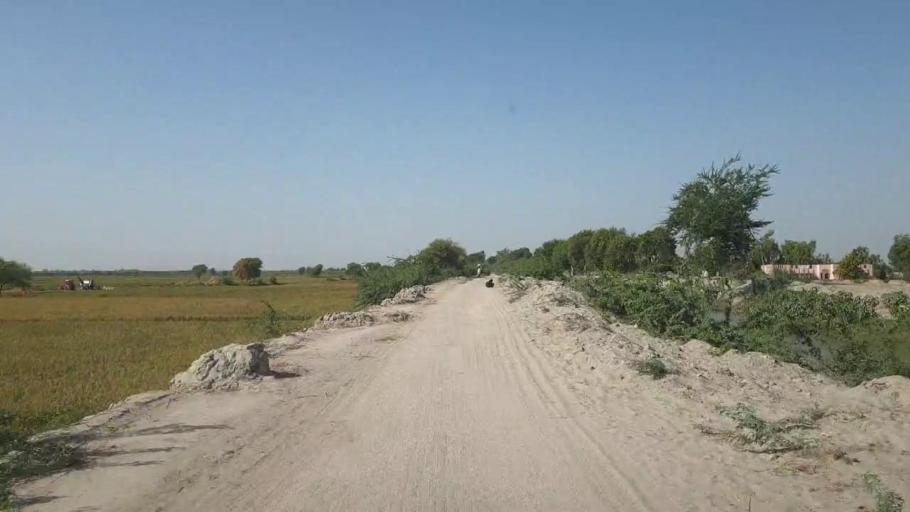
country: PK
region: Sindh
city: Kadhan
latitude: 24.5739
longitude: 68.9858
